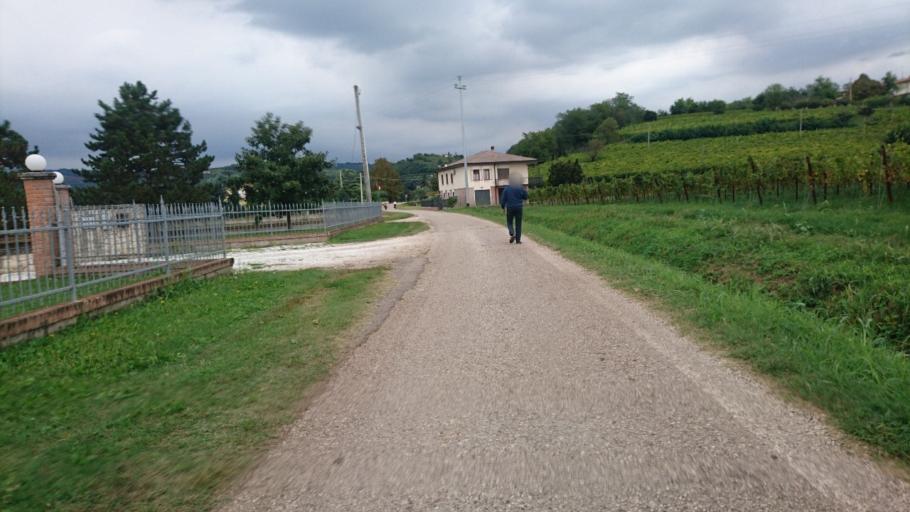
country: IT
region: Veneto
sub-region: Provincia di Vicenza
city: Gambellara
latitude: 45.4435
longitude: 11.3526
